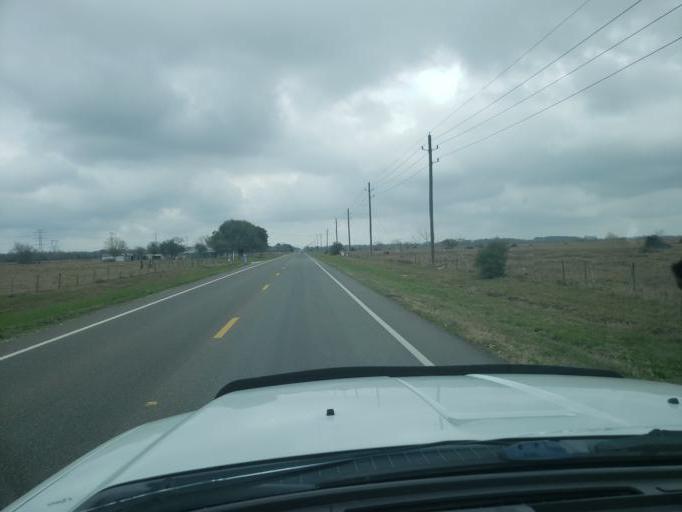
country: US
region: Texas
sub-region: Fort Bend County
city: Needville
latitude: 29.3610
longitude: -95.7650
